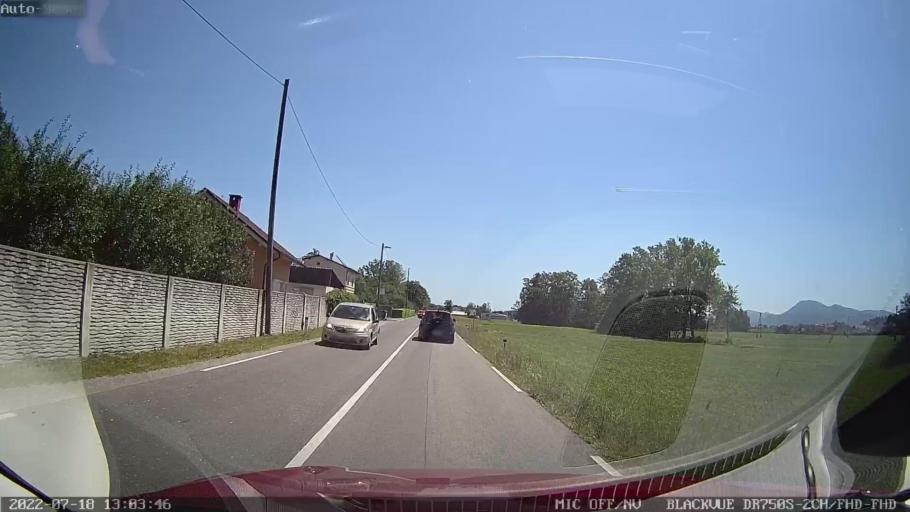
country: SI
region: Brezovica
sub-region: Opstina Ljubljana-Vic-Rudnik
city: Brezovica pri Ljubljani
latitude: 46.0487
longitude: 14.4360
